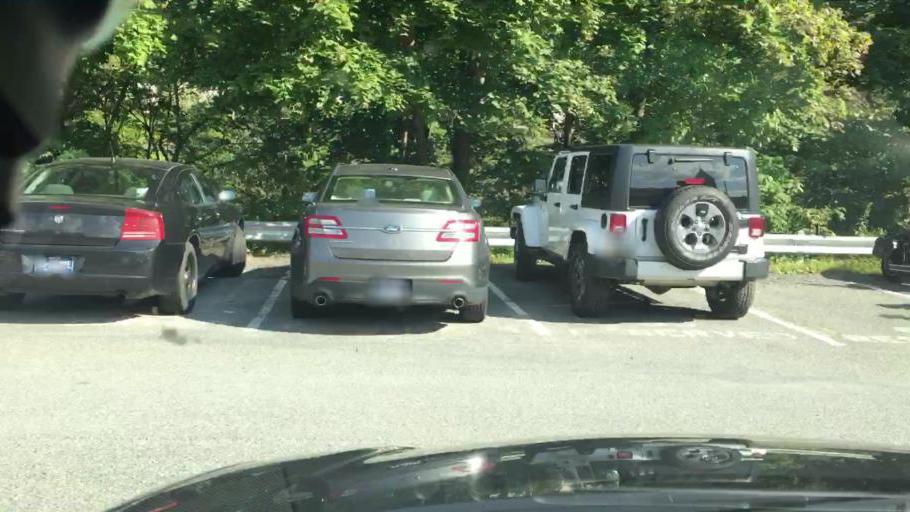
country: US
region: Pennsylvania
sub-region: Carbon County
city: Jim Thorpe
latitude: 40.8636
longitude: -75.7369
